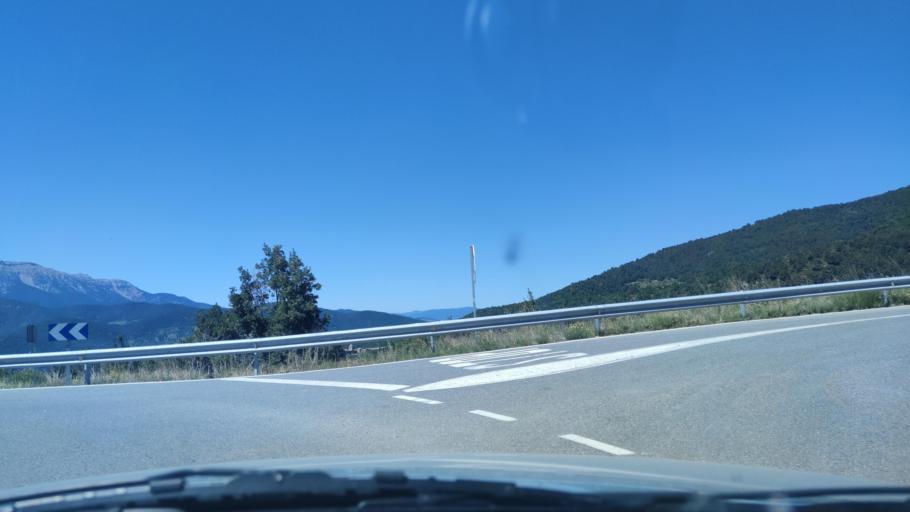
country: ES
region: Catalonia
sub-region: Provincia de Lleida
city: Lles de Cerdanya
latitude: 42.3861
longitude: 1.6769
